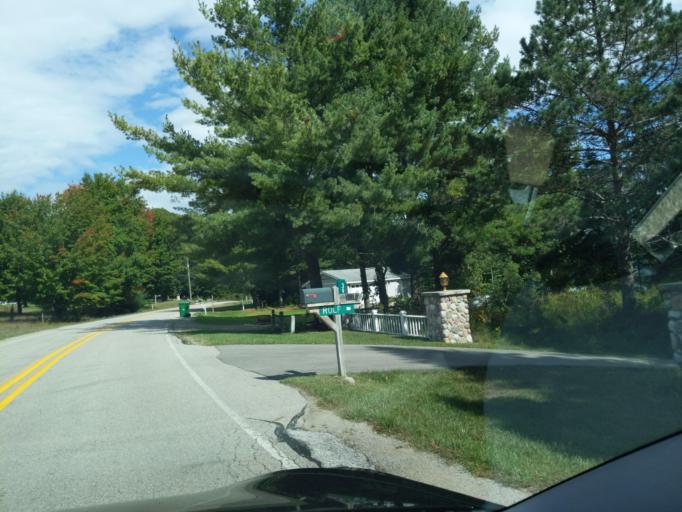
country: US
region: Michigan
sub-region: Antrim County
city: Bellaire
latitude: 44.9760
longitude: -85.3241
